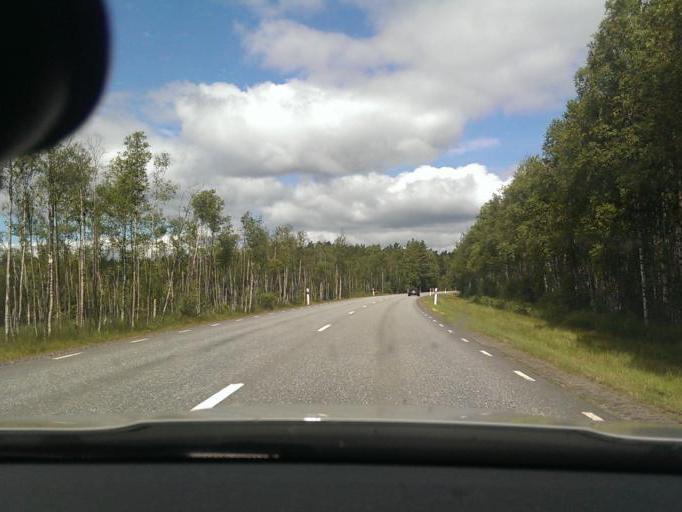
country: SE
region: Joenkoeping
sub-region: Gnosjo Kommun
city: Hillerstorp
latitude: 57.2915
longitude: 13.9373
